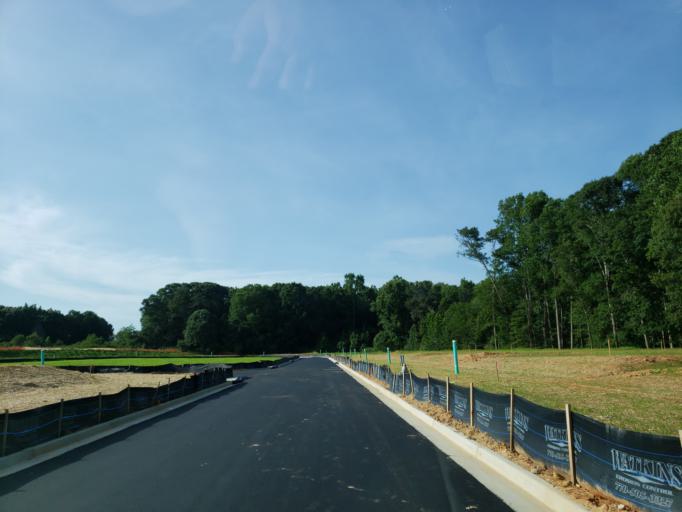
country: US
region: Georgia
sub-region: Cobb County
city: Powder Springs
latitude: 33.9082
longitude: -84.7026
